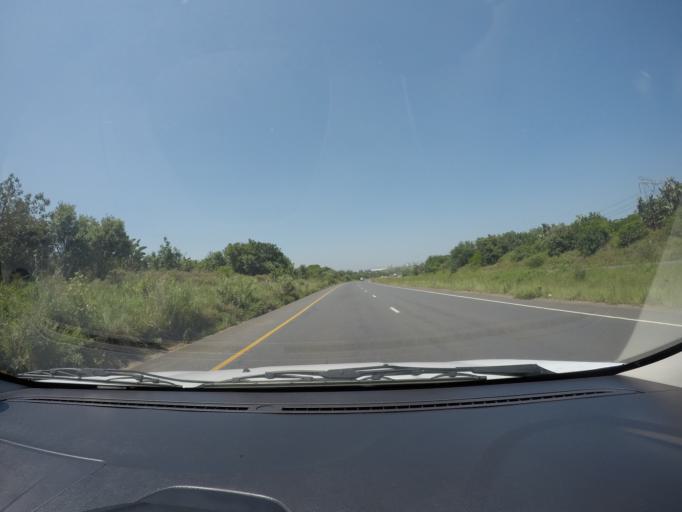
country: ZA
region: KwaZulu-Natal
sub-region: uThungulu District Municipality
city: Richards Bay
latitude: -28.7743
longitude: 32.0087
